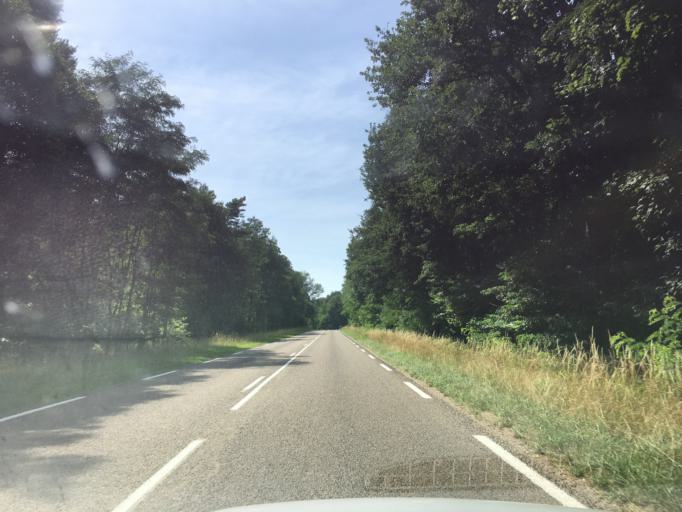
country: FR
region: Bourgogne
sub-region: Departement de l'Yonne
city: Charbuy
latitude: 47.8208
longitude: 3.4468
